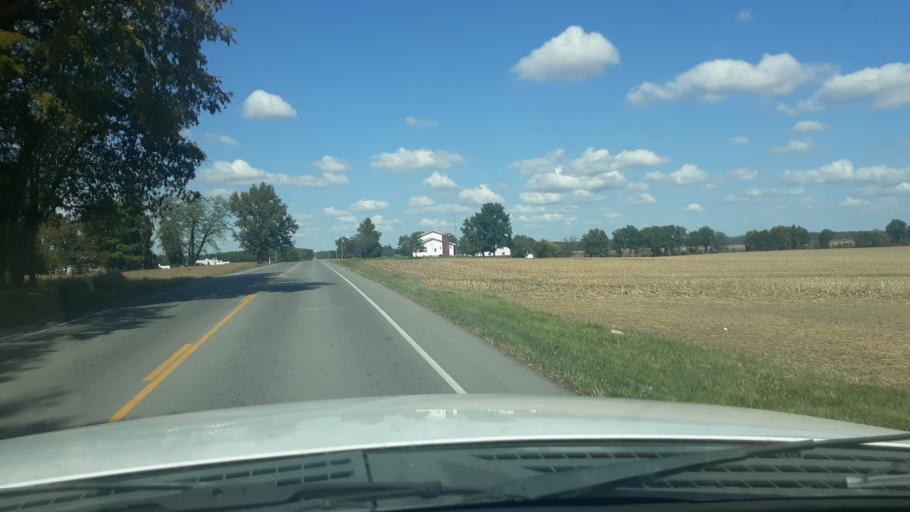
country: US
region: Illinois
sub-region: Saline County
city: Eldorado
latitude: 37.7932
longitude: -88.4848
